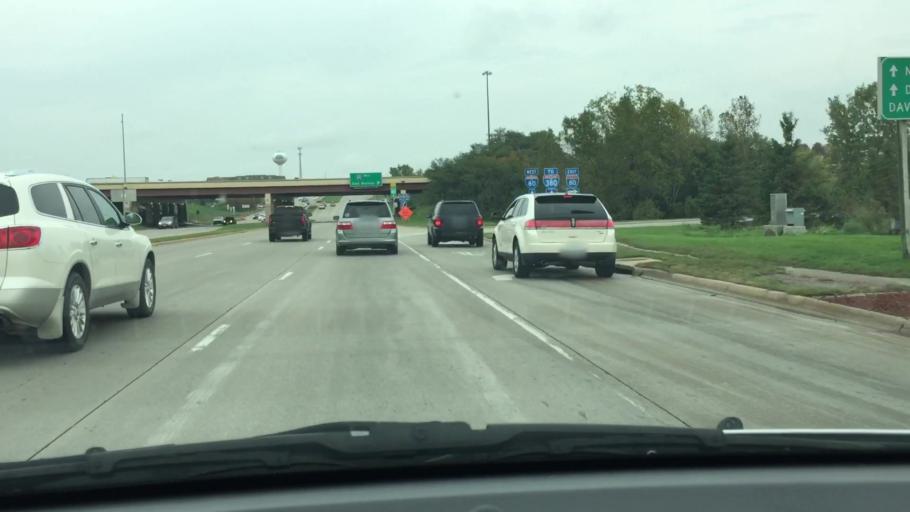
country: US
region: Iowa
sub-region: Johnson County
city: Coralville
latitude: 41.6925
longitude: -91.6084
